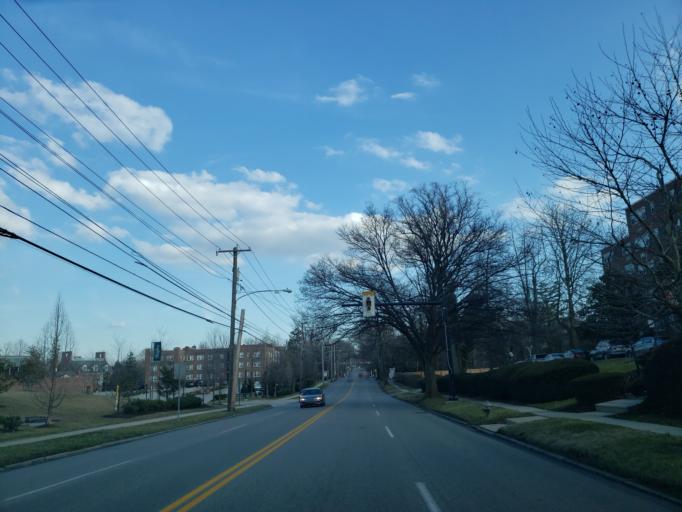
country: US
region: Pennsylvania
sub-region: Montgomery County
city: Bryn Mawr
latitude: 40.0241
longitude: -75.3175
